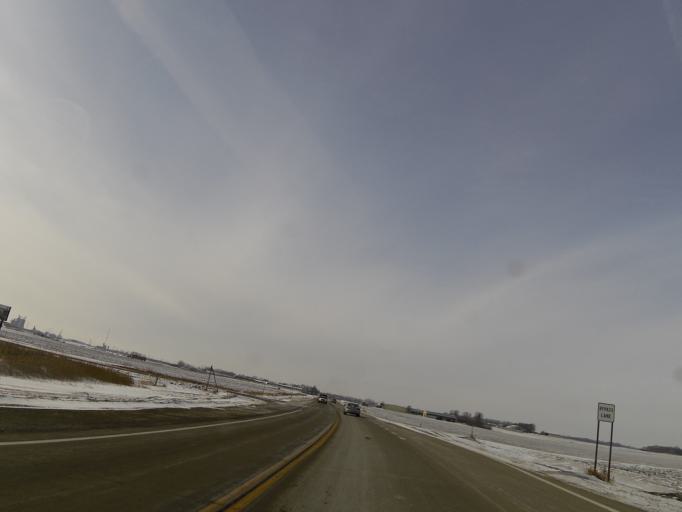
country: US
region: Minnesota
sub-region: McLeod County
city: Hutchinson
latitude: 44.8962
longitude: -94.3265
